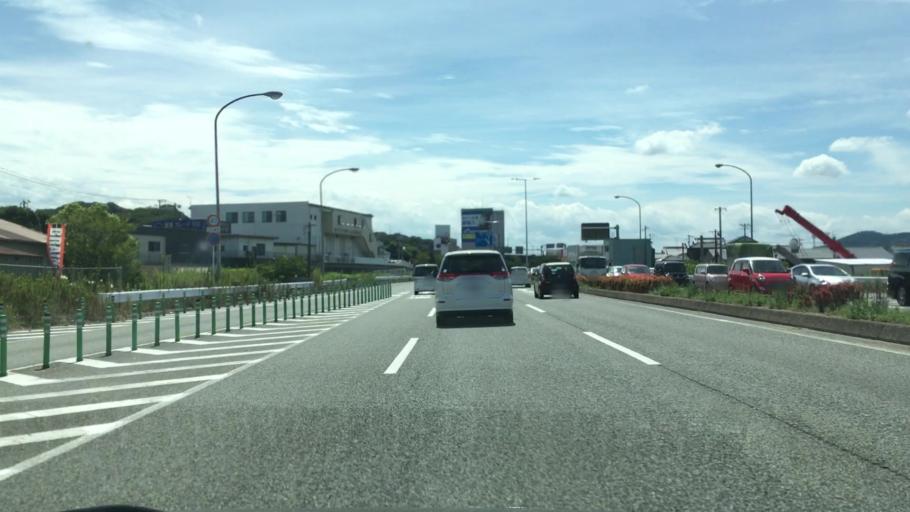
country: JP
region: Fukuoka
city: Onojo
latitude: 33.5298
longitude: 130.4930
